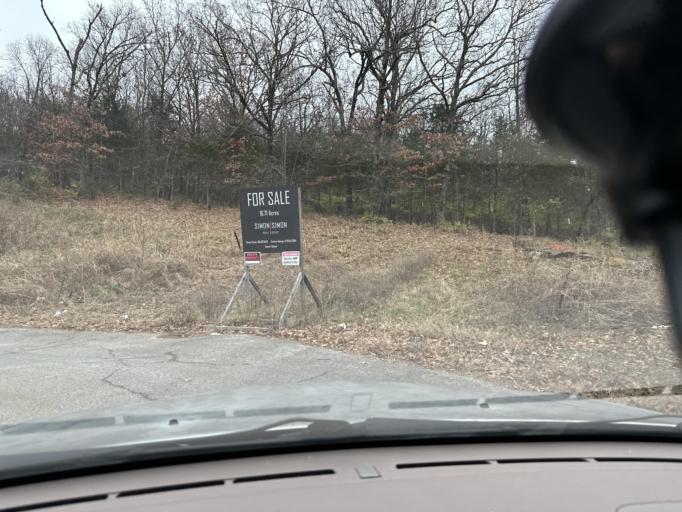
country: US
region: Arkansas
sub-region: Washington County
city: Fayetteville
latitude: 36.0917
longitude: -94.1515
